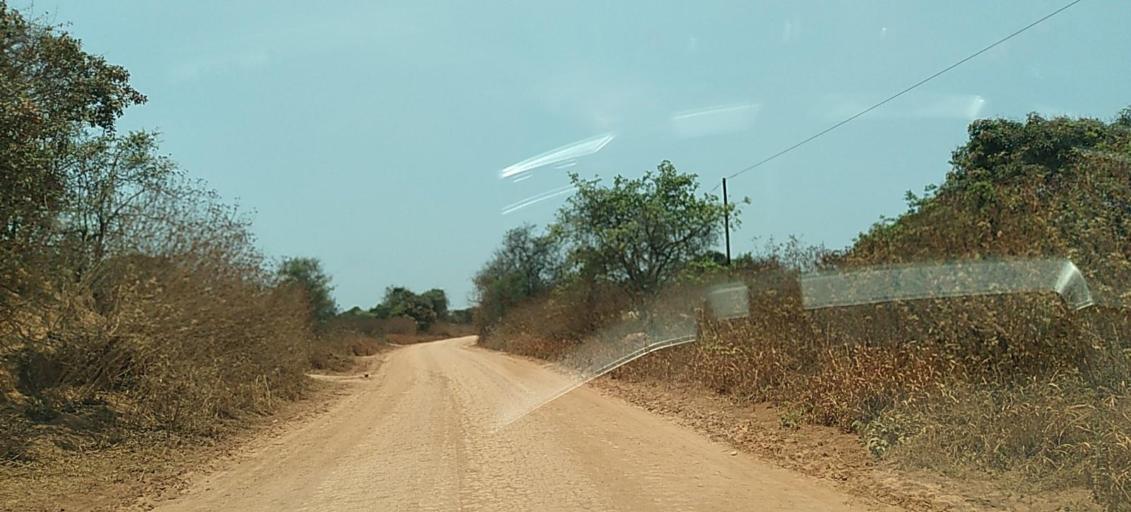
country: CD
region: Katanga
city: Kipushi
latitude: -11.7823
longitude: 27.1814
